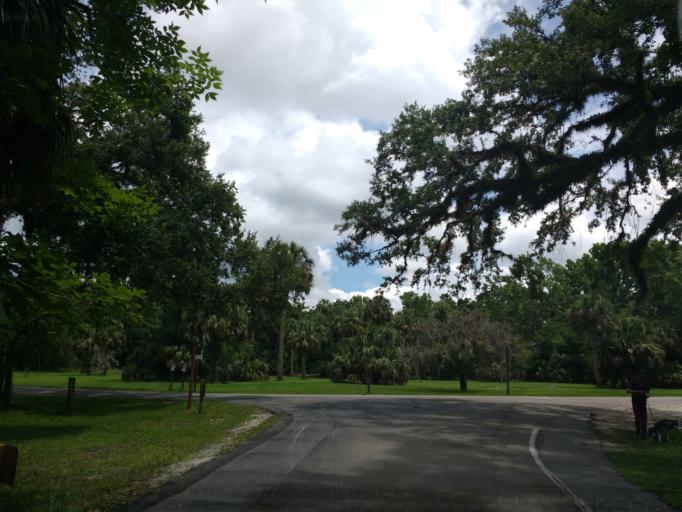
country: US
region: Florida
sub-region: Highlands County
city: Sebring
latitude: 27.4707
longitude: -81.5412
